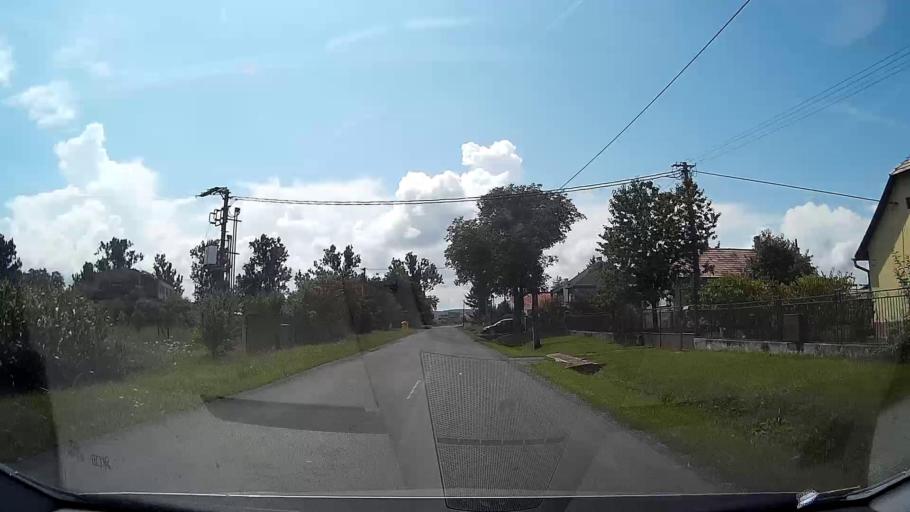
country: SK
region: Banskobystricky
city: Fil'akovo
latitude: 48.3189
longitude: 19.8121
